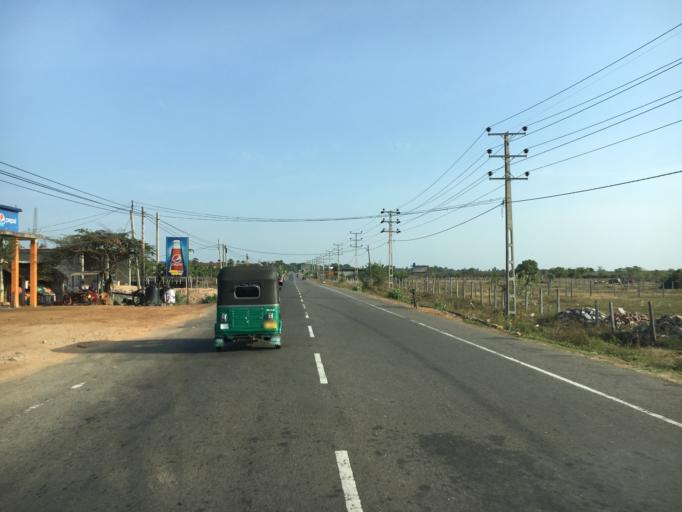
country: LK
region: Eastern Province
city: Eravur Town
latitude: 7.9347
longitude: 81.5104
